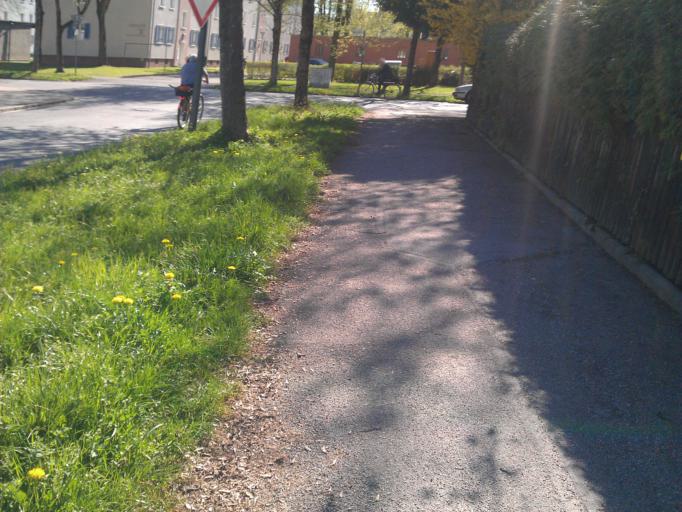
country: DE
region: Bavaria
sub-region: Swabia
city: Augsburg
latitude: 48.3589
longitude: 10.9129
